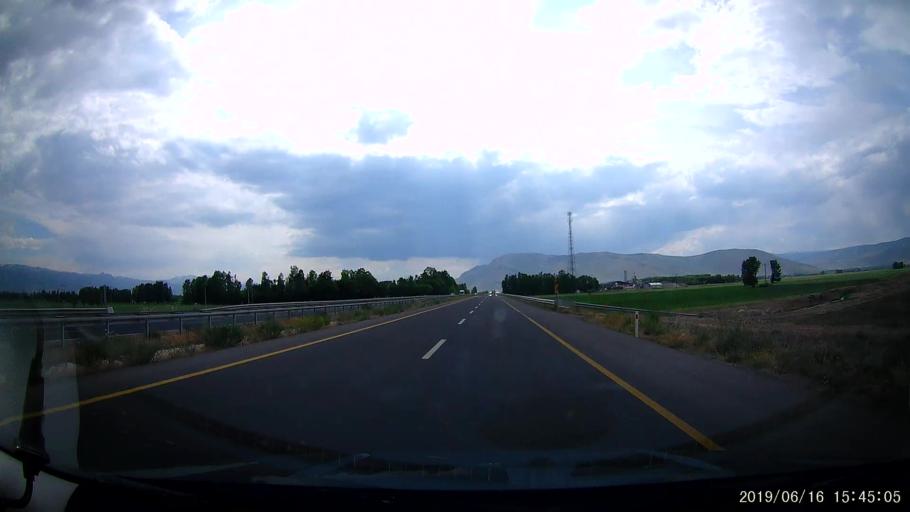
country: TR
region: Erzurum
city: Koprukoy
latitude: 39.9878
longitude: 41.7751
